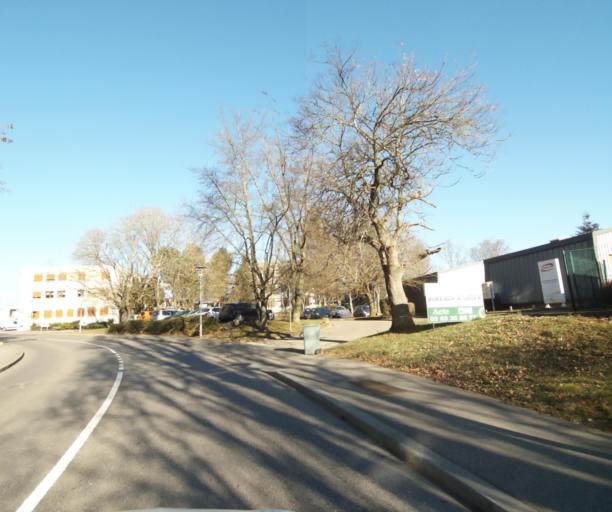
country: FR
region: Lorraine
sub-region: Departement de Meurthe-et-Moselle
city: Laxou
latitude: 48.7025
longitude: 6.1338
